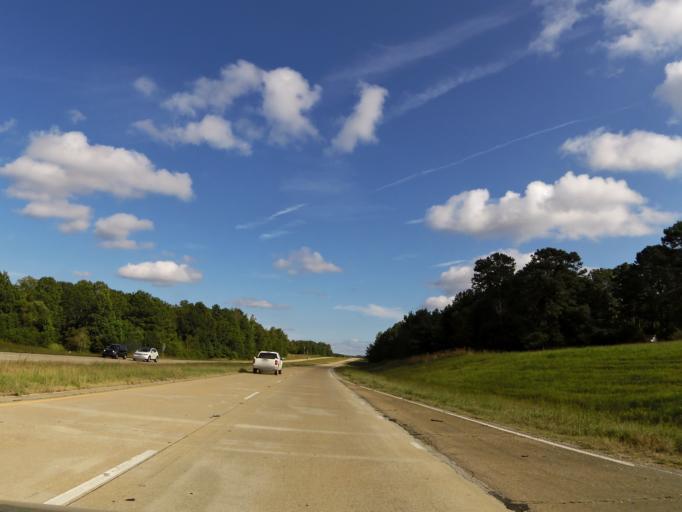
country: US
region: Mississippi
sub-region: Tishomingo County
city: Iuka
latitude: 34.8236
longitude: -88.2962
